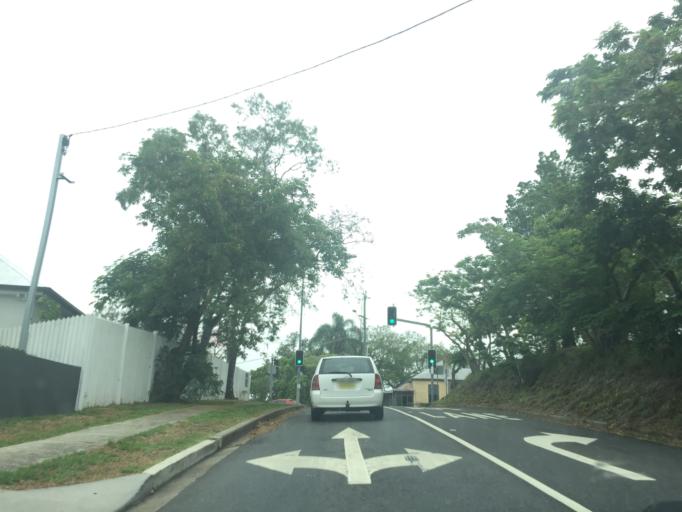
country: AU
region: Queensland
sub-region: Brisbane
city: Milton
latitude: -27.4568
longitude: 152.9854
